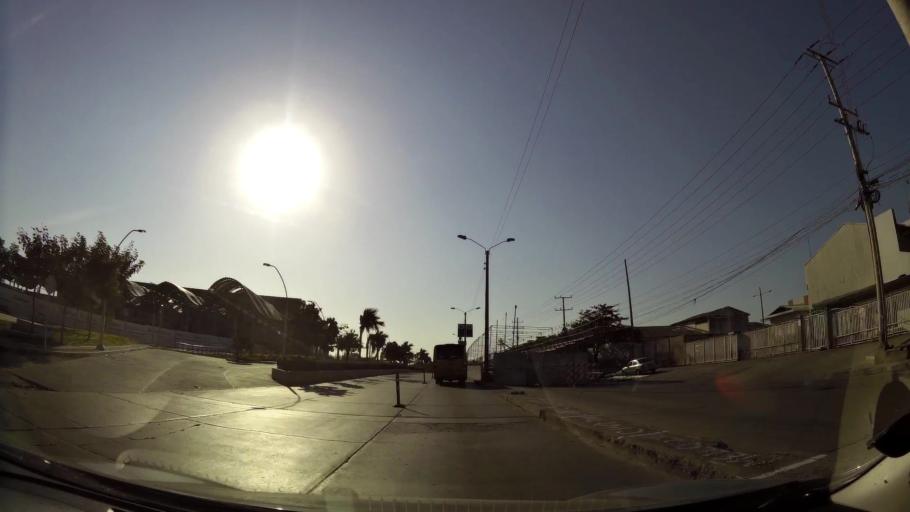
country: CO
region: Atlantico
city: Barranquilla
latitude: 11.0240
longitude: -74.8017
